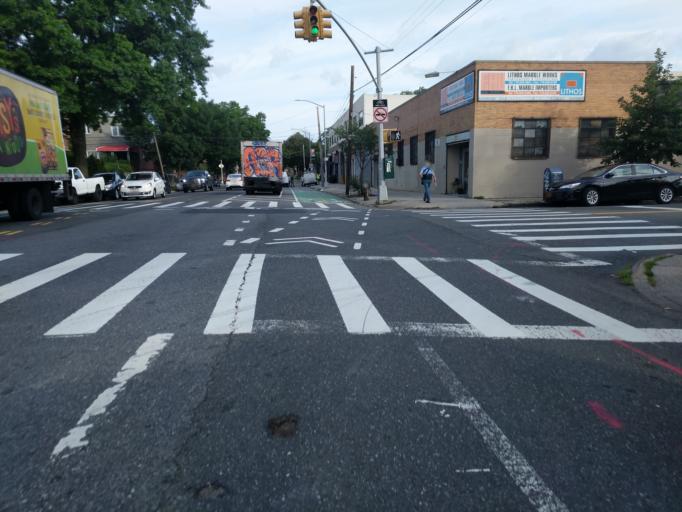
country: US
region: New York
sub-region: Queens County
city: Long Island City
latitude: 40.7775
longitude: -73.9029
